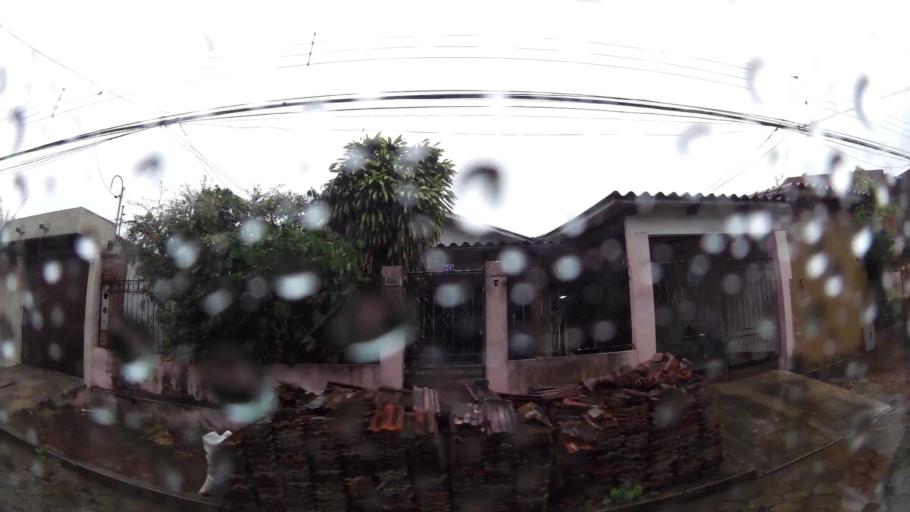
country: BO
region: Santa Cruz
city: Santa Cruz de la Sierra
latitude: -17.7984
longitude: -63.1655
